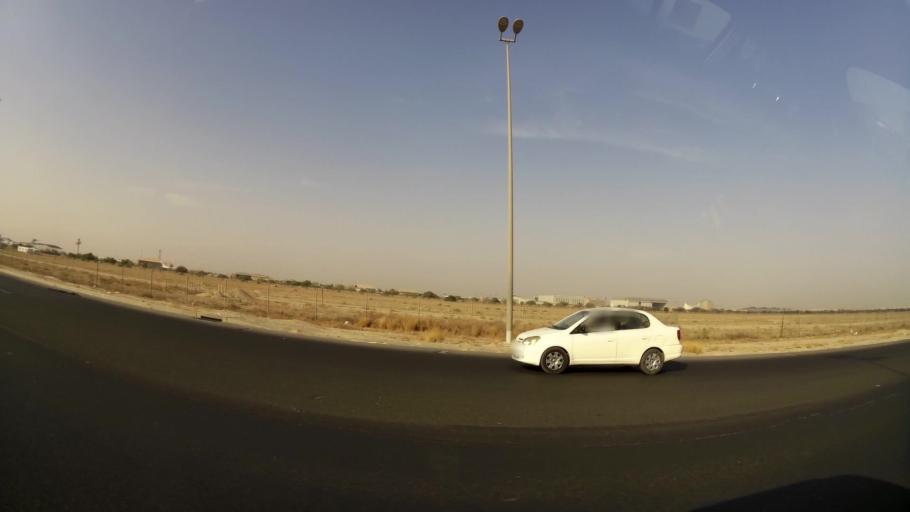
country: KW
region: Al Farwaniyah
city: Janub as Surrah
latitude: 29.2379
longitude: 47.9916
